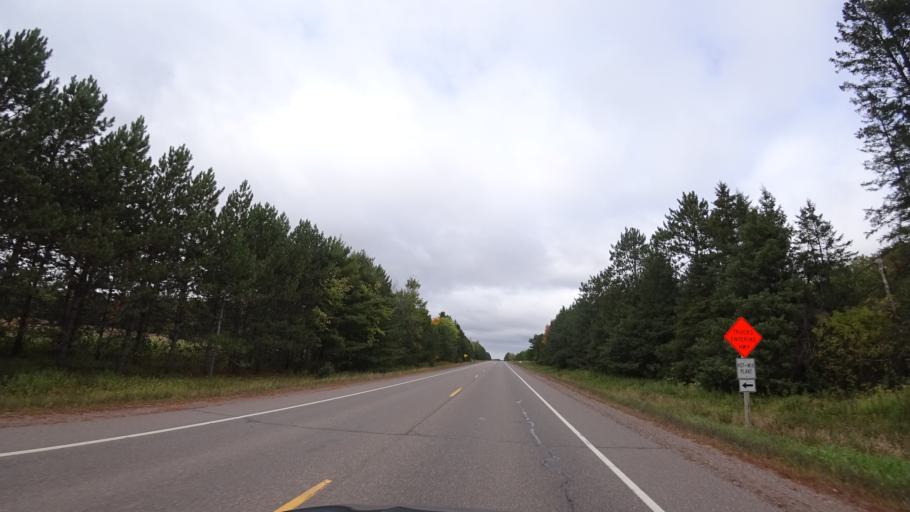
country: US
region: Wisconsin
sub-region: Rusk County
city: Ladysmith
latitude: 45.5147
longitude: -91.1115
